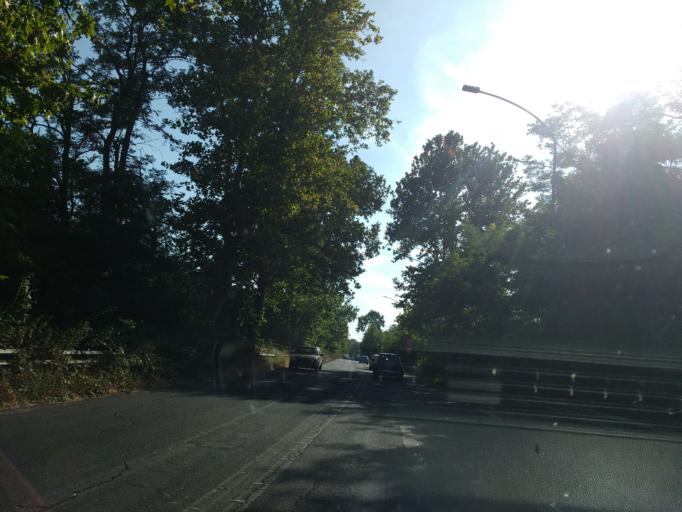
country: IT
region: Latium
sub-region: Citta metropolitana di Roma Capitale
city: Vitinia
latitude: 41.7914
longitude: 12.3811
